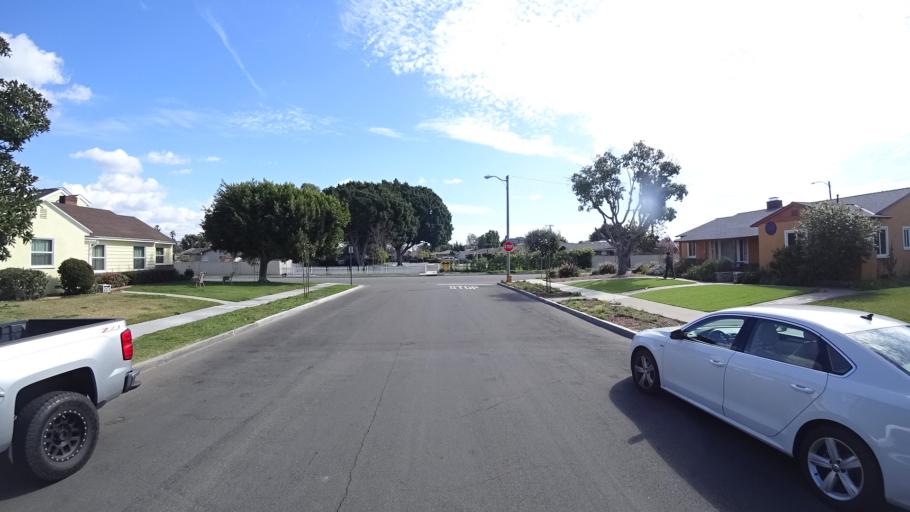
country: US
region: California
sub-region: Orange County
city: Anaheim
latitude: 33.8406
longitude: -117.9238
